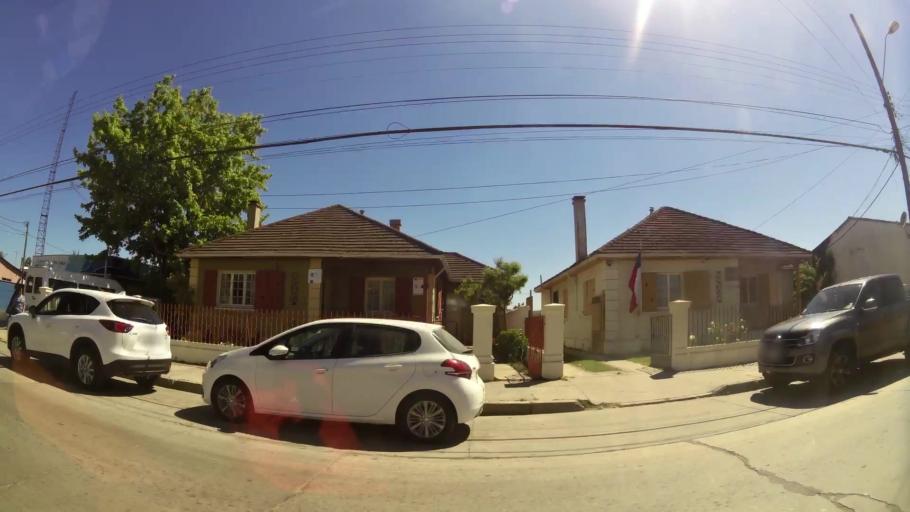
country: CL
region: Valparaiso
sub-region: Provincia de Marga Marga
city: Quilpue
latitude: -33.3228
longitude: -71.4059
